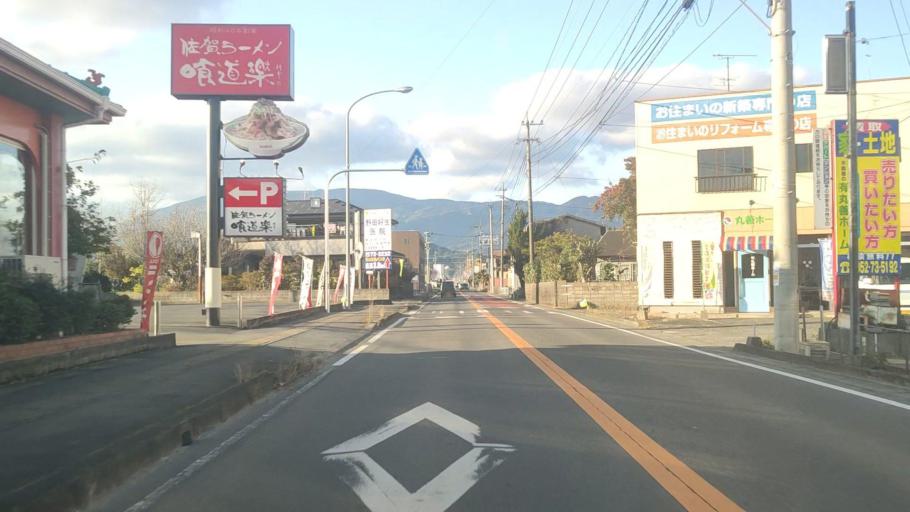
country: JP
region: Saga Prefecture
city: Saga-shi
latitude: 33.2820
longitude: 130.2113
